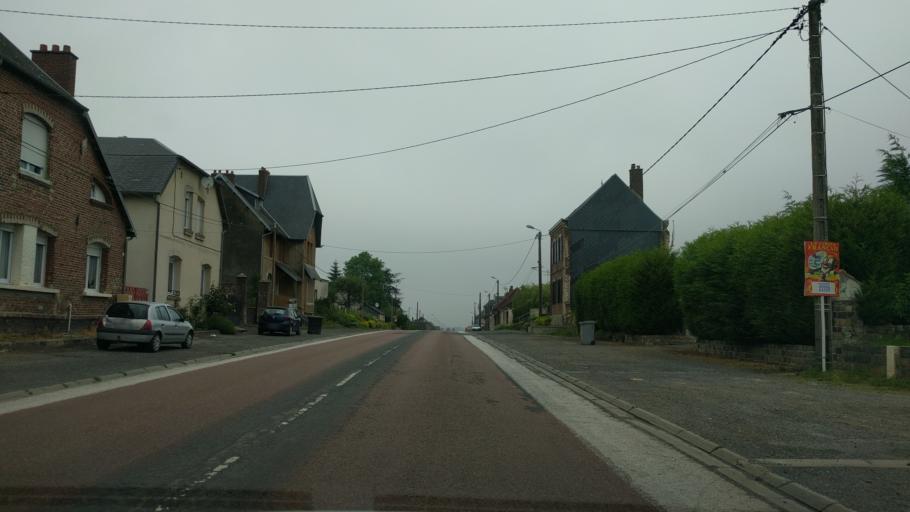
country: FR
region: Picardie
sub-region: Departement de la Somme
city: Moislains
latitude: 50.0295
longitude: 2.9123
